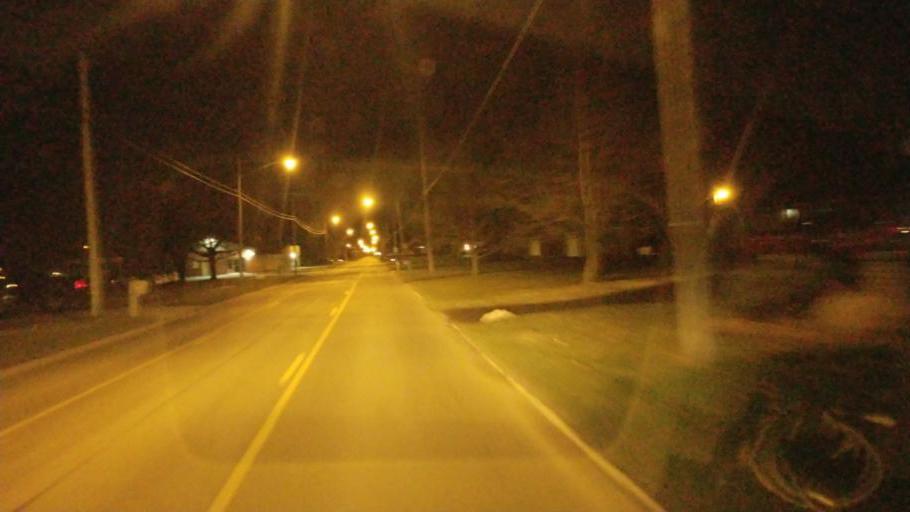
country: US
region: Ohio
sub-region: Crawford County
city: Bucyrus
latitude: 40.7940
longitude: -82.9772
